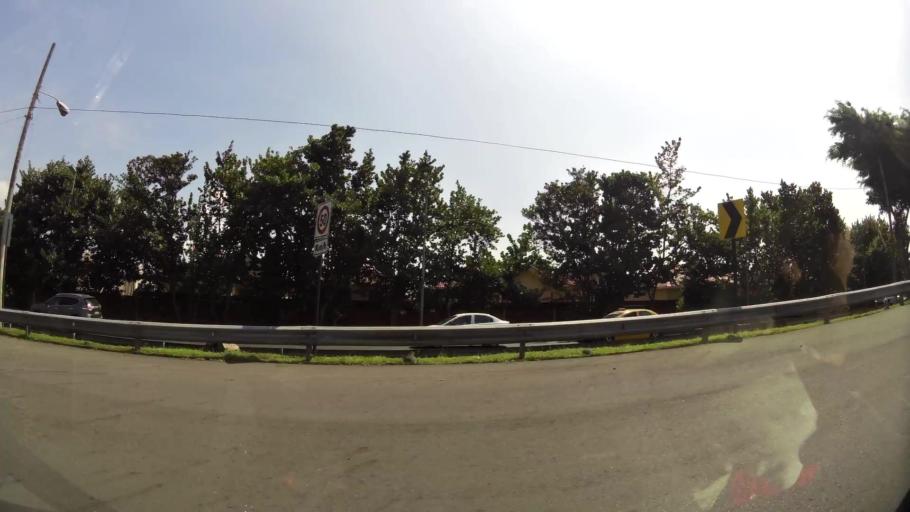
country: EC
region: Guayas
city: Eloy Alfaro
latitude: -2.1513
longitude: -79.8658
